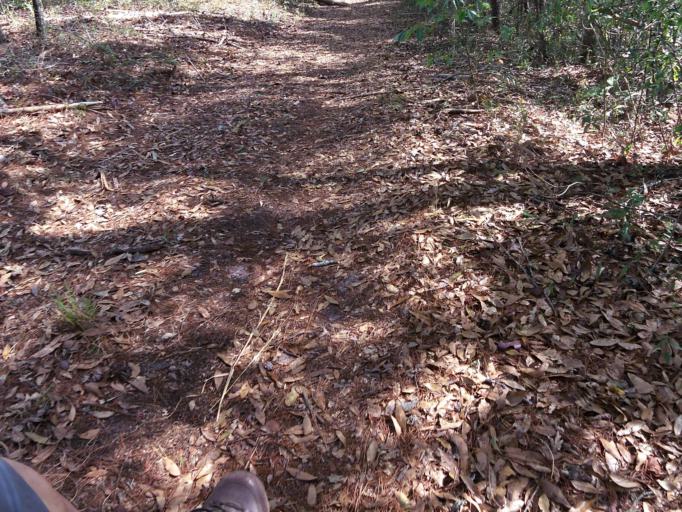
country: US
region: Florida
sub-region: Putnam County
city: Interlachen
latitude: 29.7581
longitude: -81.8197
